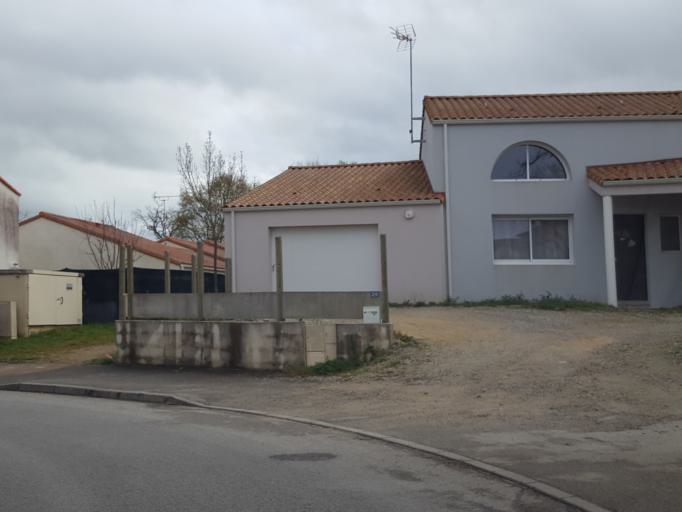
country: FR
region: Pays de la Loire
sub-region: Departement de la Vendee
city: La Roche-sur-Yon
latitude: 46.6675
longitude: -1.3969
